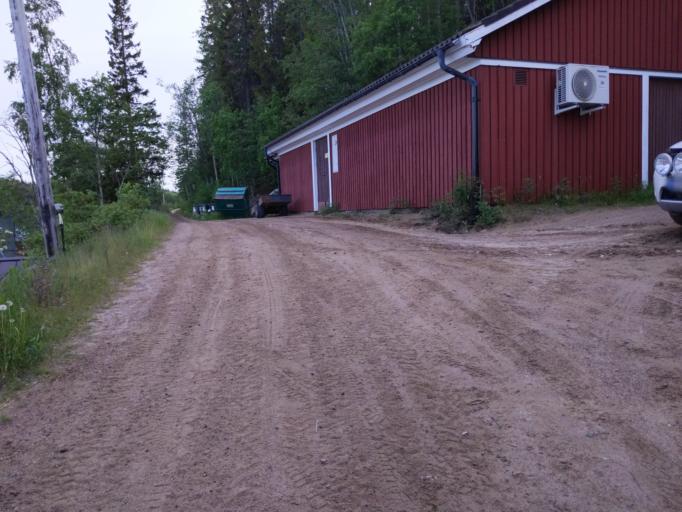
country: SE
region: Vaesternorrland
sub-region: OErnskoeldsviks Kommun
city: Kopmanholmen
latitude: 63.0194
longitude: 18.6456
